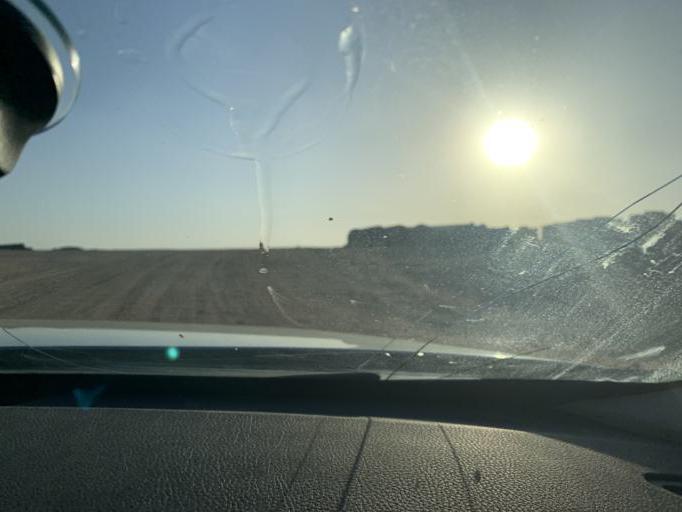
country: EG
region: Muhafazat al Qalyubiyah
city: Al Khankah
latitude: 30.0225
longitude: 31.6774
